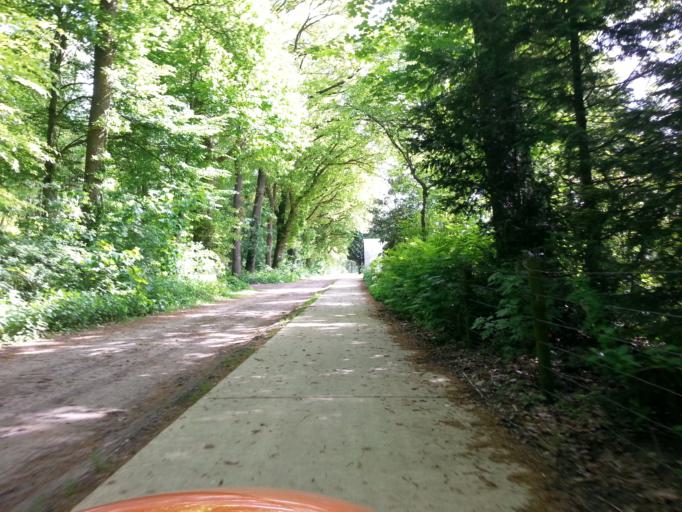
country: NL
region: Gelderland
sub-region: Gemeente Ede
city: Lunteren
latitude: 52.0798
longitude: 5.6563
